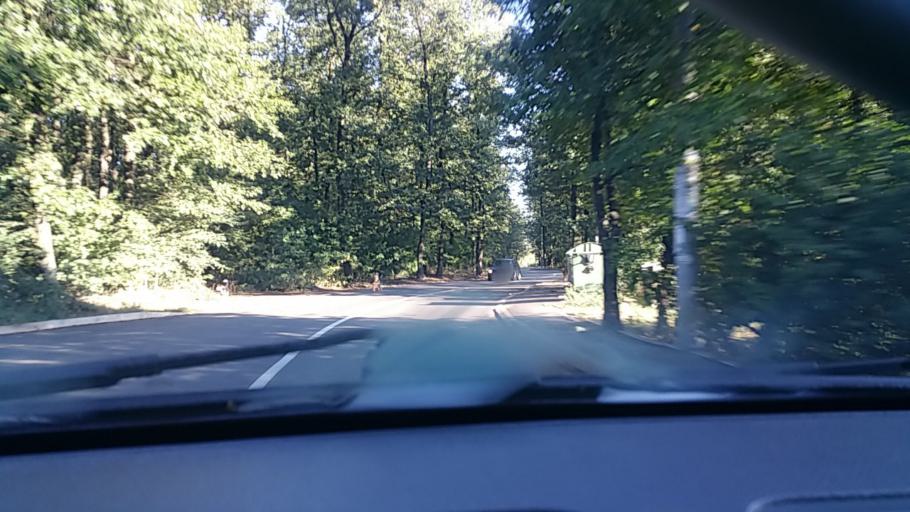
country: RS
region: Central Serbia
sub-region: Belgrade
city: Rakovica
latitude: 44.7383
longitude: 20.4634
